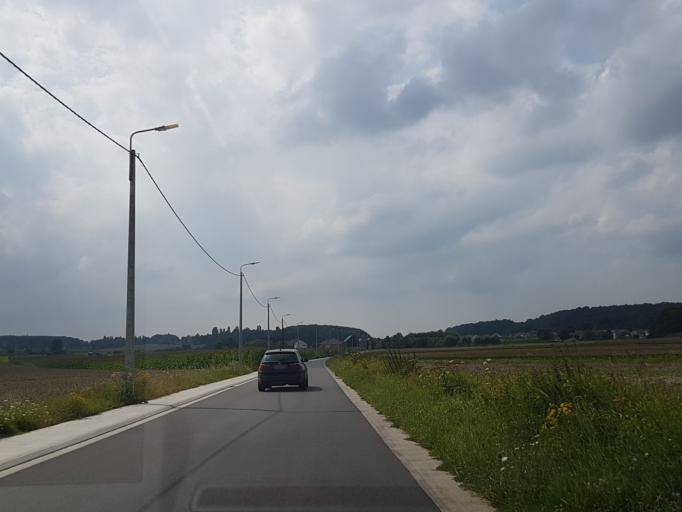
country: BE
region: Flanders
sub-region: Provincie Vlaams-Brabant
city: Kortenberg
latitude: 50.8768
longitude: 4.5649
